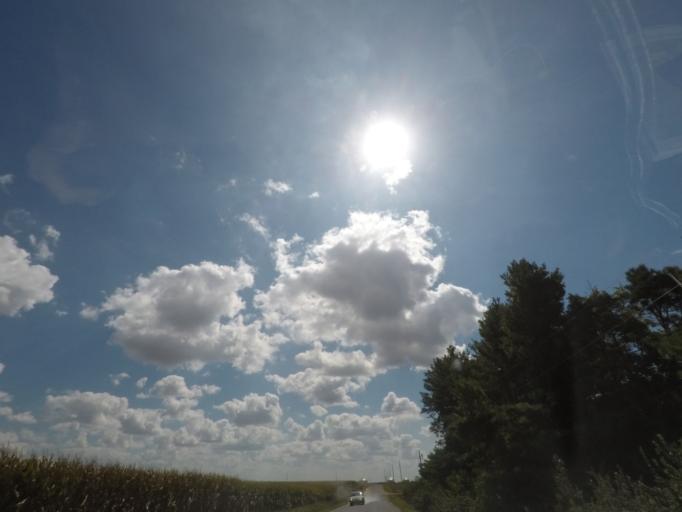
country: US
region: Iowa
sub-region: Story County
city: Nevada
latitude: 42.0392
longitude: -93.3621
